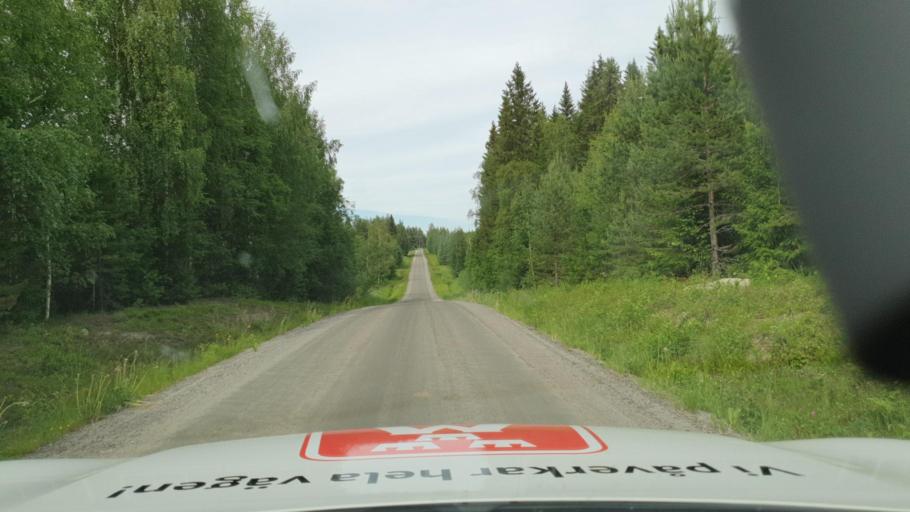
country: SE
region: Vaesterbotten
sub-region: Skelleftea Kommun
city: Viken
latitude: 64.5034
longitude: 20.9281
